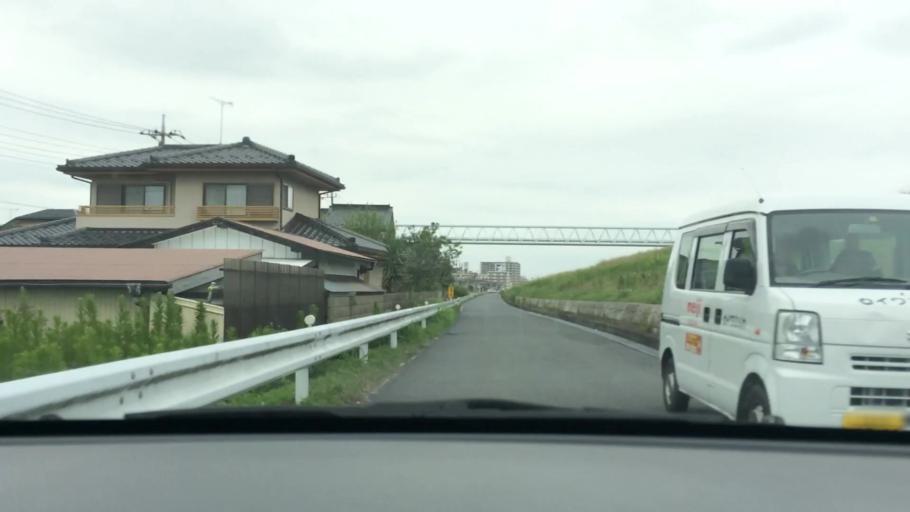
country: JP
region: Chiba
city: Nagareyama
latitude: 35.8359
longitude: 139.8863
